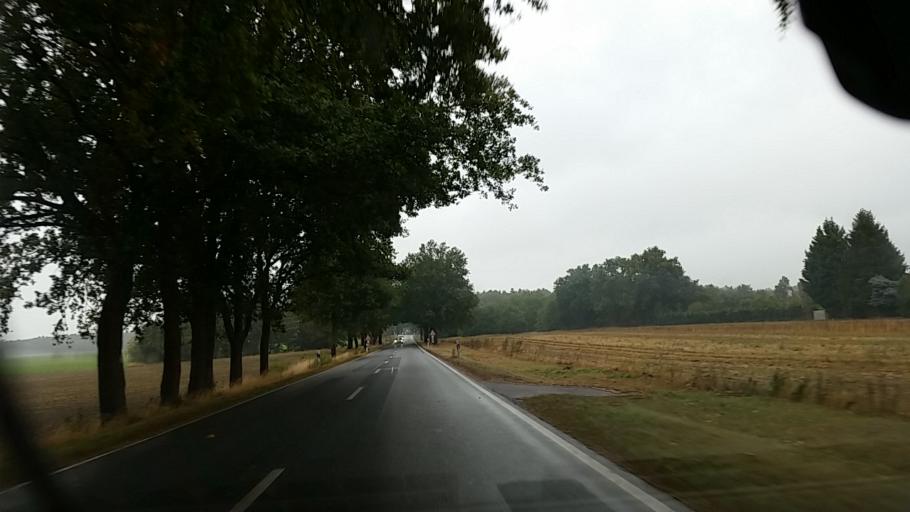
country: DE
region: Lower Saxony
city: Wittingen
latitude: 52.7672
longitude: 10.7108
